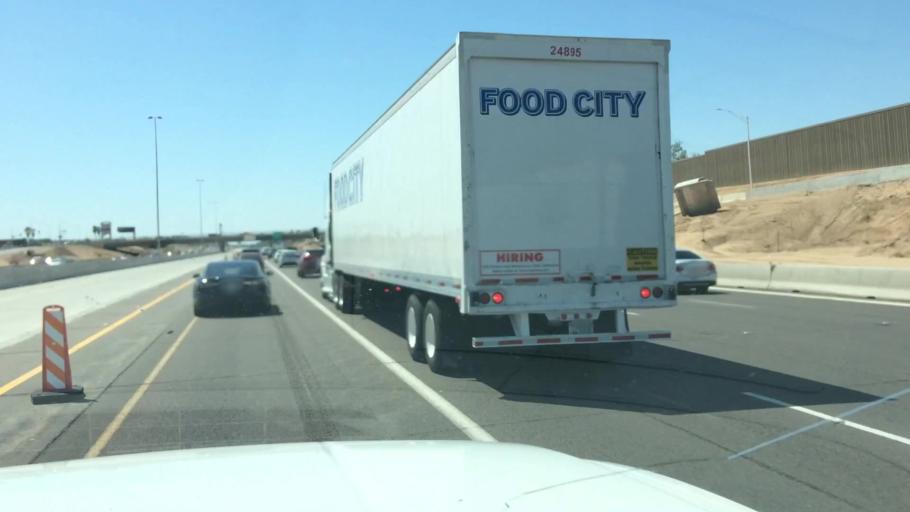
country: US
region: Arizona
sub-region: Maricopa County
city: Tolleson
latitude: 33.4611
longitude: -112.2011
